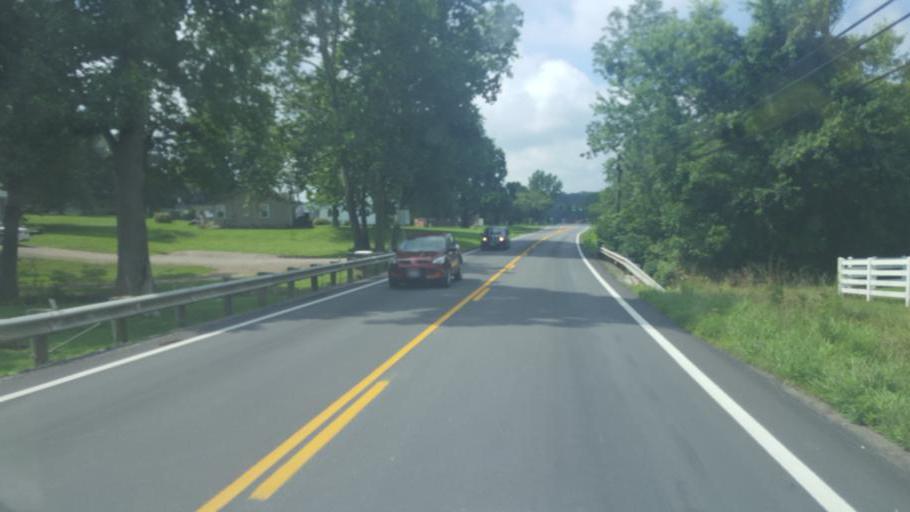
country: US
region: Ohio
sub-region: Fairfield County
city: Lancaster
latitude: 39.7544
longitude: -82.5824
